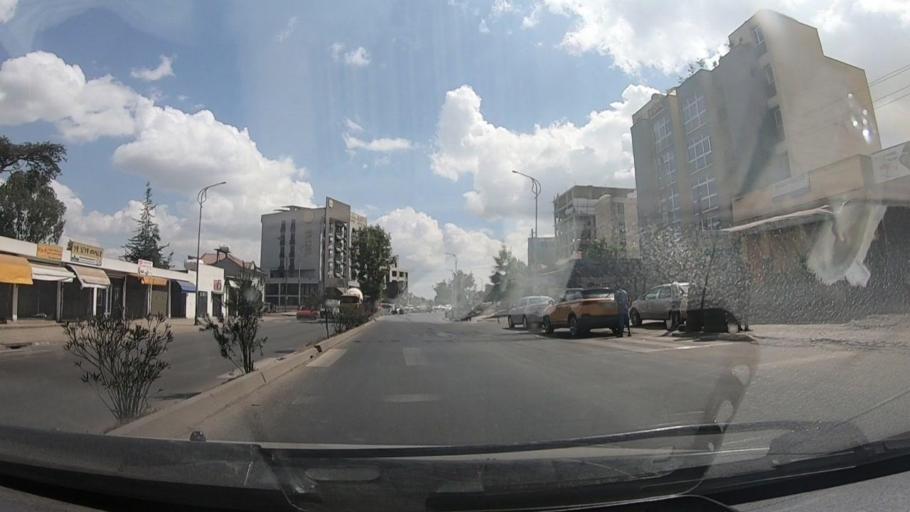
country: ET
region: Adis Abeba
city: Addis Ababa
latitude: 8.9809
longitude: 38.7208
